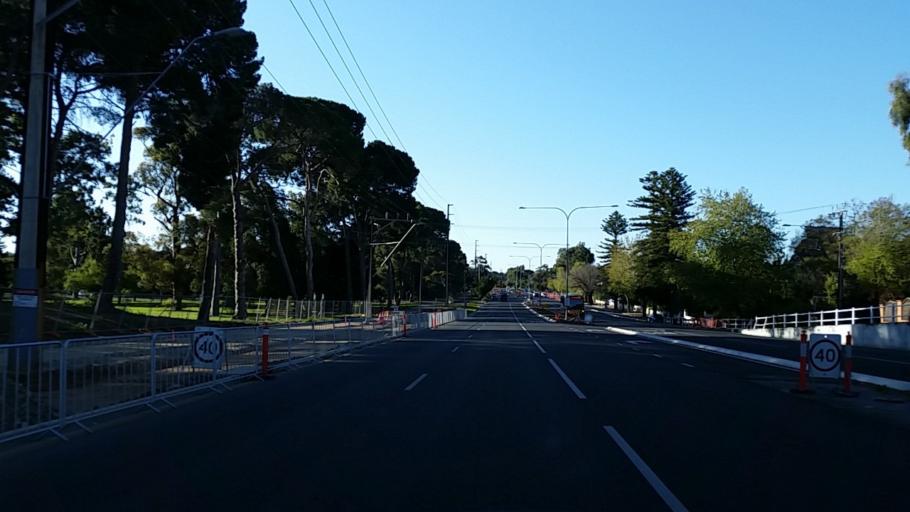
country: AU
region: South Australia
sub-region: Adelaide
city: Adelaide
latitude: -34.9137
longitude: 138.6137
